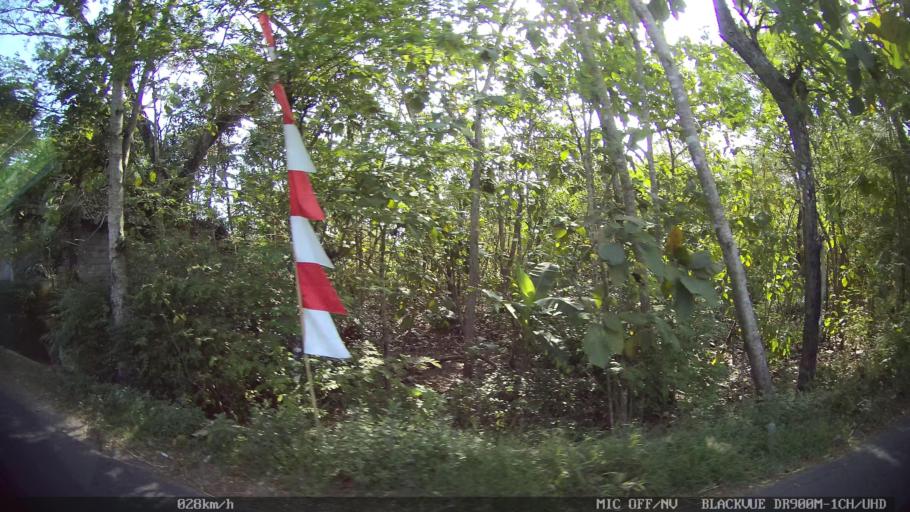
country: ID
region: Daerah Istimewa Yogyakarta
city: Kasihan
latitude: -7.8323
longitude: 110.3234
